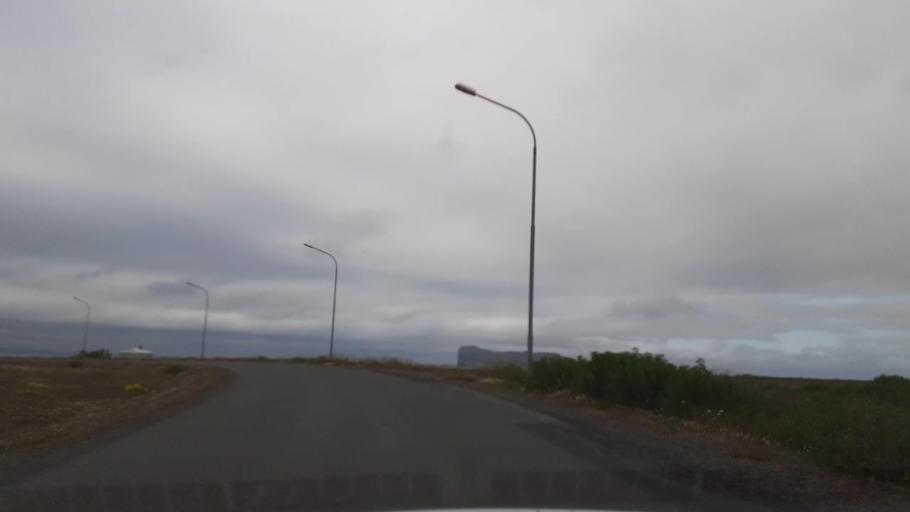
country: IS
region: Northwest
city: Saudarkrokur
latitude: 65.9005
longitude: -19.4163
